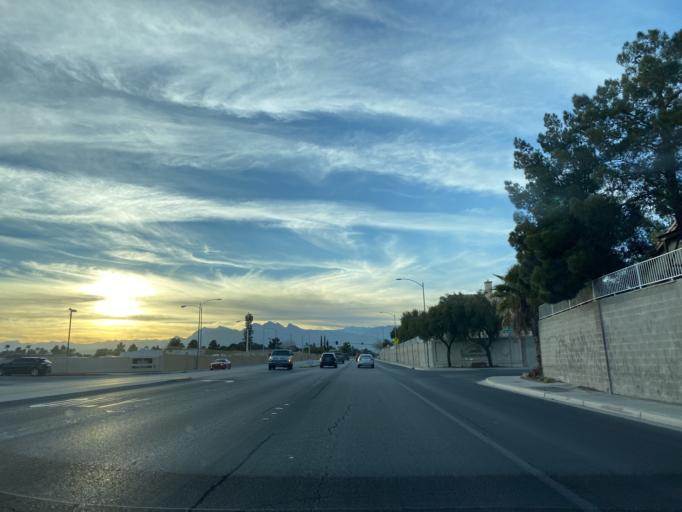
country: US
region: Nevada
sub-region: Clark County
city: North Las Vegas
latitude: 36.2613
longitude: -115.2140
